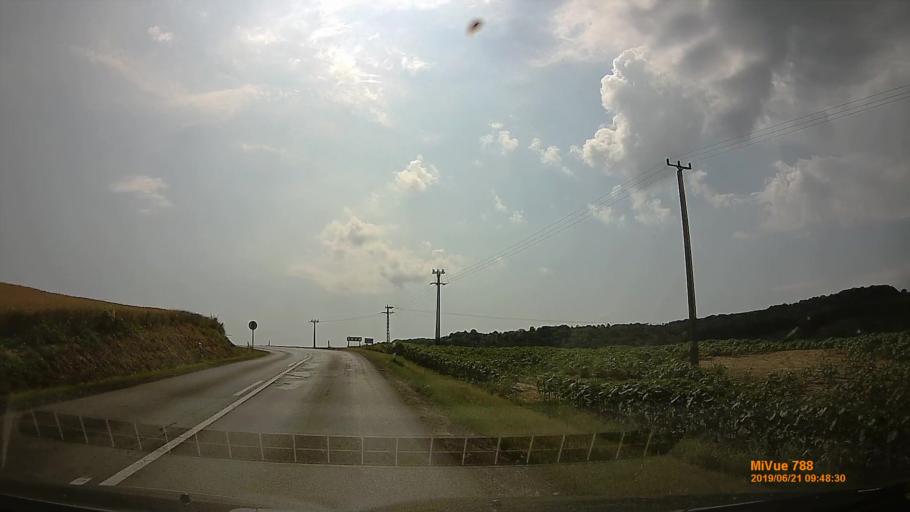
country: HU
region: Baranya
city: Sasd
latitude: 46.2675
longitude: 18.0303
